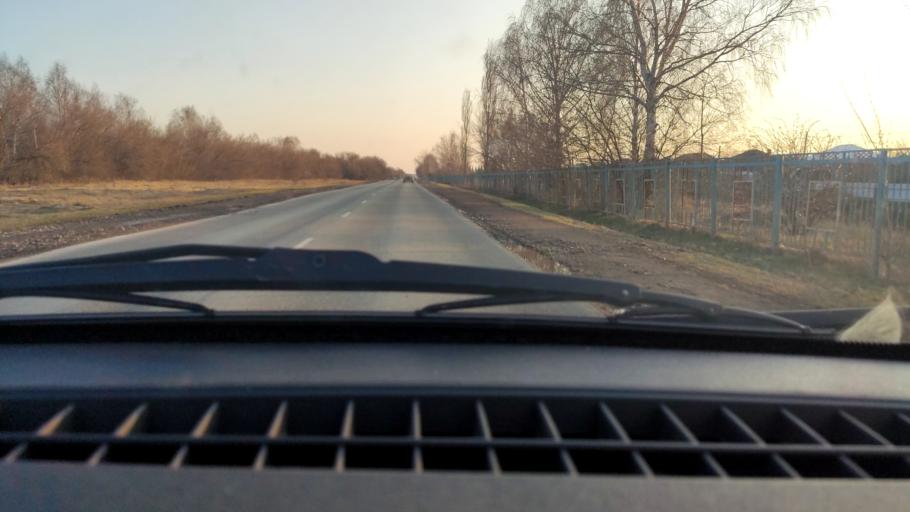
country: RU
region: Bashkortostan
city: Davlekanovo
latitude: 54.2994
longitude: 55.1307
